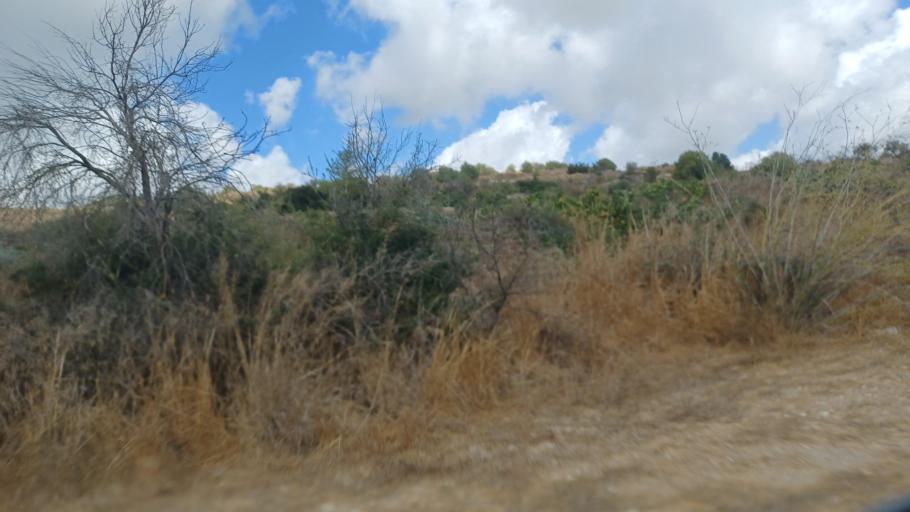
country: CY
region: Pafos
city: Mesogi
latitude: 34.8416
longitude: 32.5409
